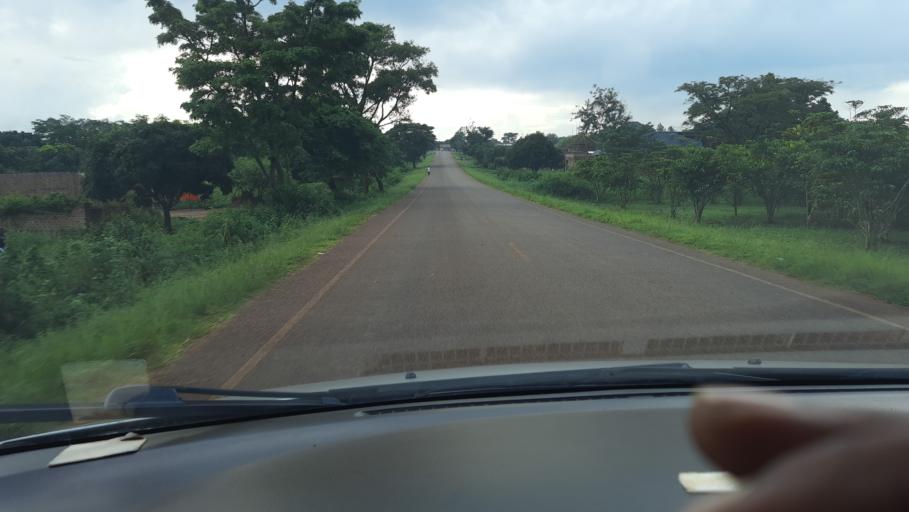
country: UG
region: Central Region
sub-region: Nakasongola District
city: Nakasongola
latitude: 1.3258
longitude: 32.4258
